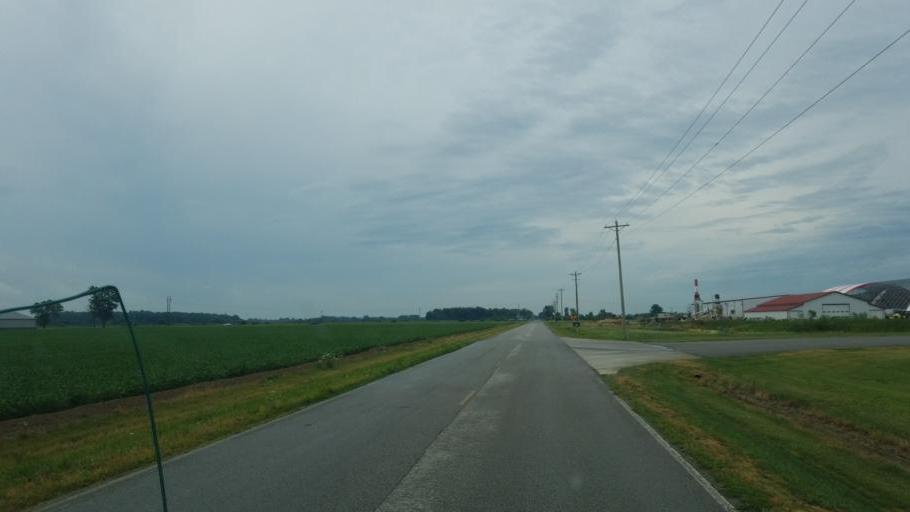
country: US
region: Ohio
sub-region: Defiance County
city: Hicksville
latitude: 41.2997
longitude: -84.6896
